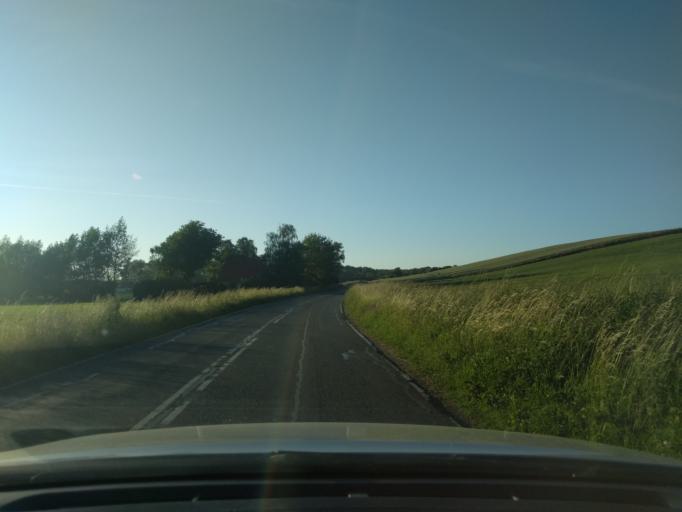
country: DK
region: South Denmark
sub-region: Kerteminde Kommune
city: Kerteminde
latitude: 55.5230
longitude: 10.6539
